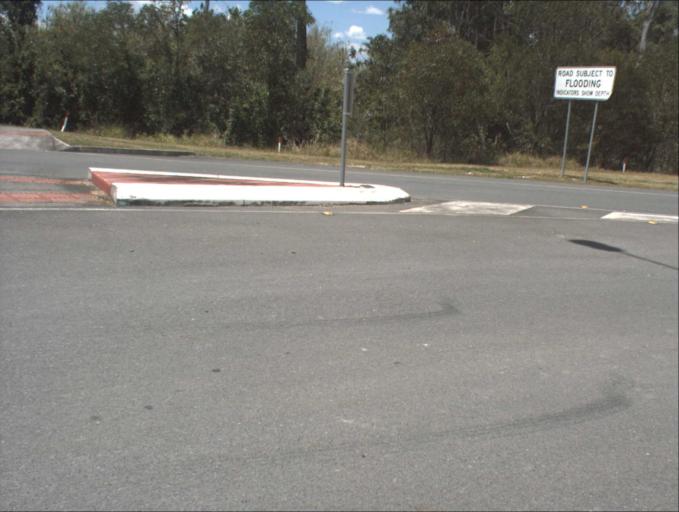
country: AU
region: Queensland
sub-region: Logan
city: Woodridge
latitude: -27.6564
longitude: 153.0908
